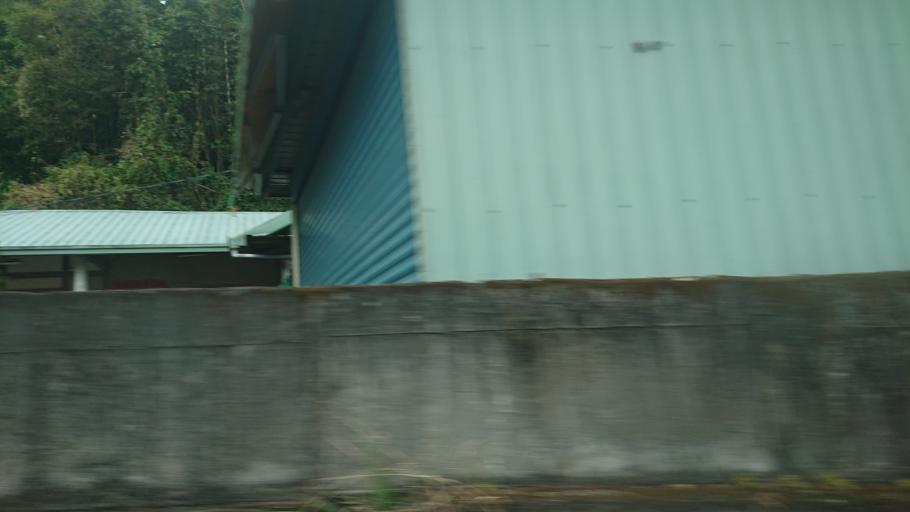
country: TW
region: Taiwan
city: Lugu
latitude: 23.5842
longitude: 120.6952
